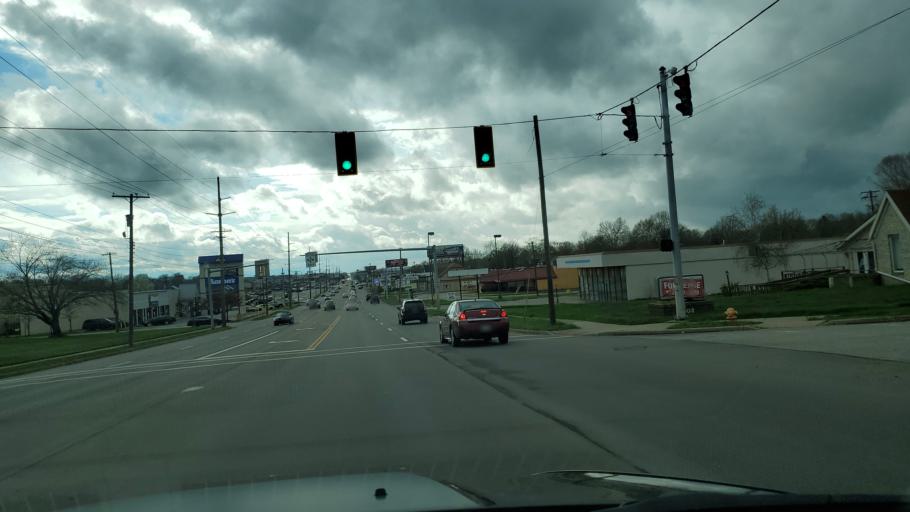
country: US
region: Ohio
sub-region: Mahoning County
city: Boardman
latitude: 41.0245
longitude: -80.6657
